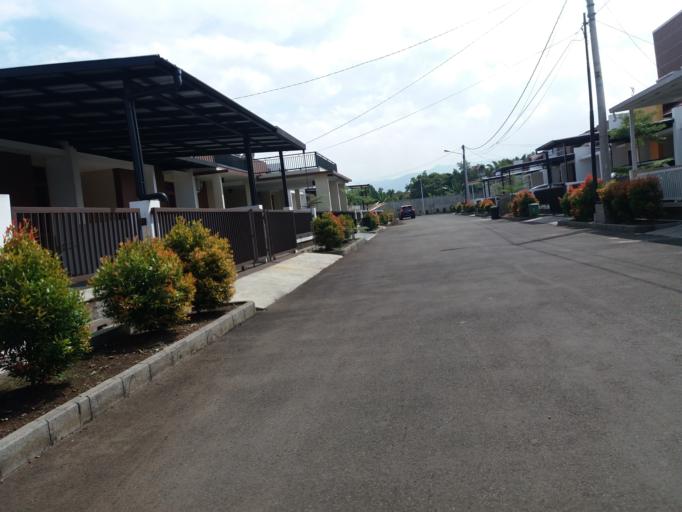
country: ID
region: West Java
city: Bandung
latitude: -6.9215
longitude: 107.6662
